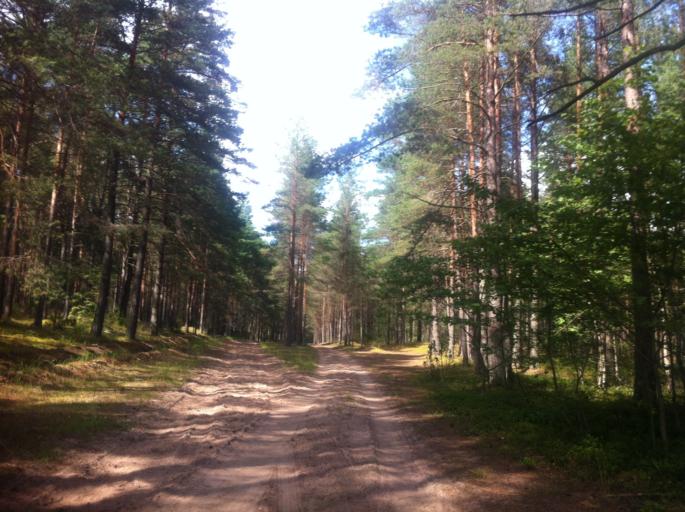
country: RU
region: Pskov
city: Izborsk
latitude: 57.8253
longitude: 27.9389
